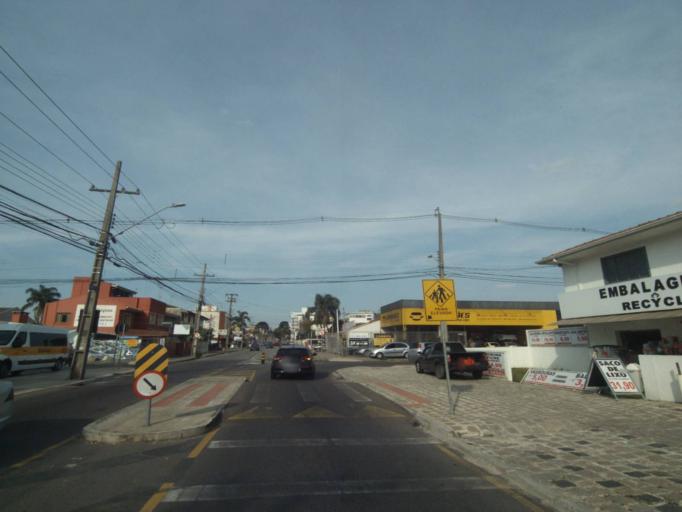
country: BR
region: Parana
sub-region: Curitiba
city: Curitiba
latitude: -25.4591
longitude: -49.3174
